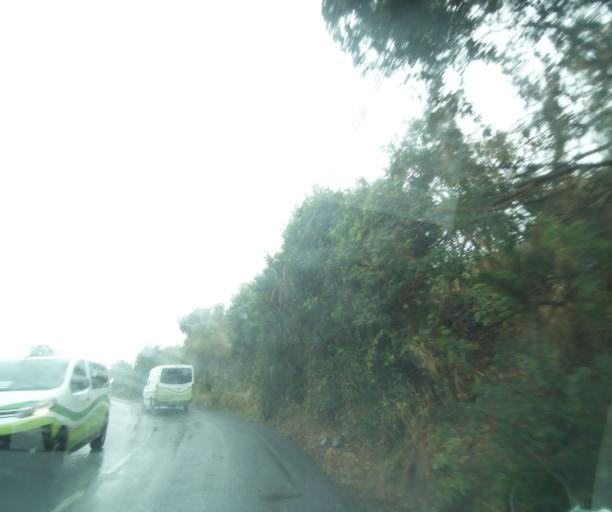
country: RE
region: Reunion
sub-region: Reunion
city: Saint-Paul
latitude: -21.0124
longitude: 55.3115
